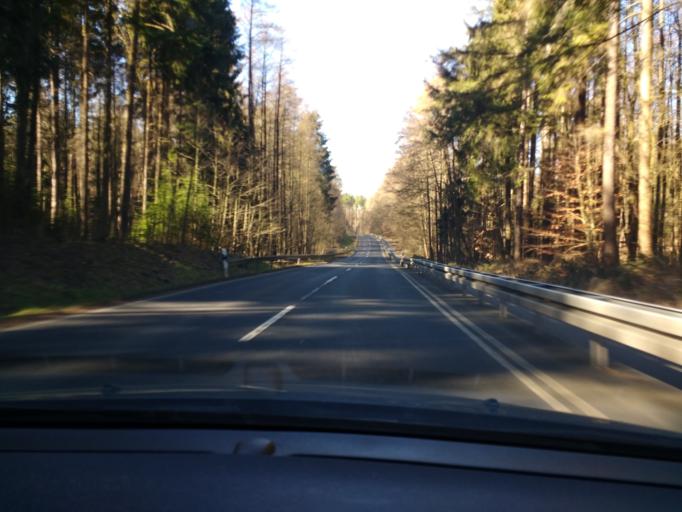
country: DE
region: Bavaria
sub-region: Regierungsbezirk Unterfranken
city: Alzenau in Unterfranken
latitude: 50.1283
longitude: 9.0776
